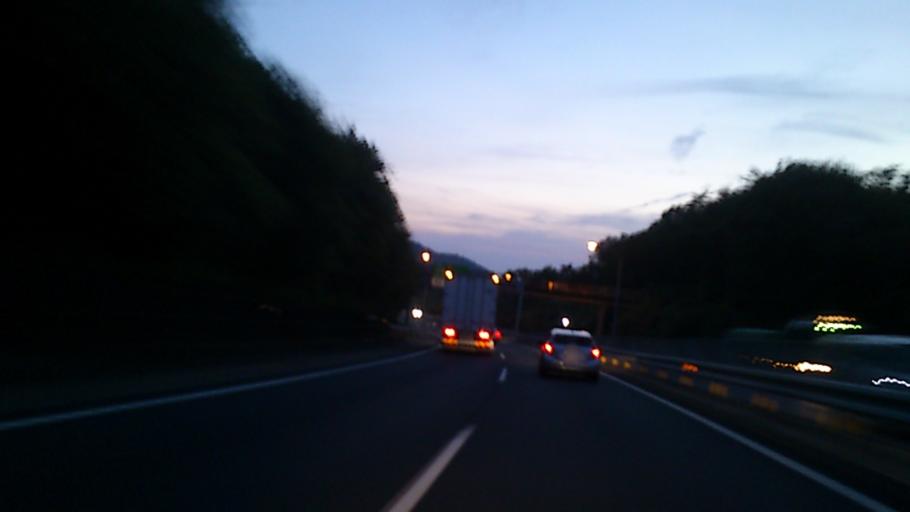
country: JP
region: Gifu
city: Inuyama
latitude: 35.3317
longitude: 137.0323
